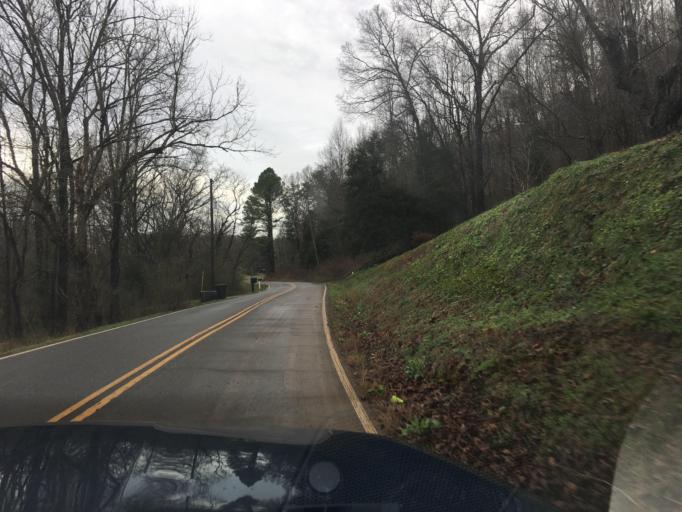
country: US
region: Tennessee
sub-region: McMinn County
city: Englewood
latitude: 35.3794
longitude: -84.4373
